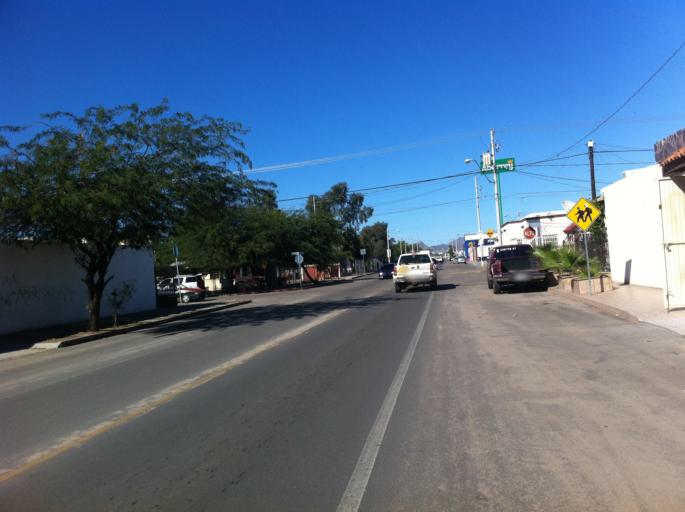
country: MX
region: Sonora
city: Hermosillo
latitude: 29.1074
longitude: -111.0055
